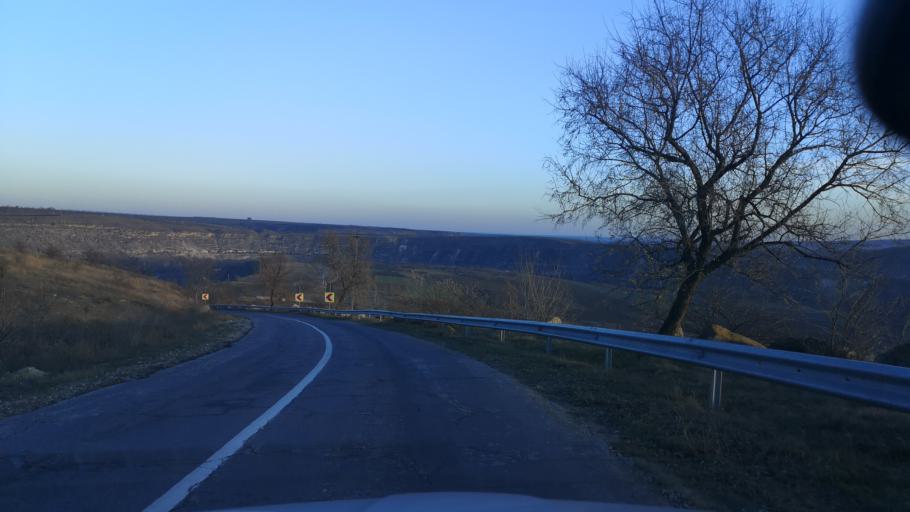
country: MD
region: Telenesti
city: Cocieri
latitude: 47.3103
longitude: 28.9672
